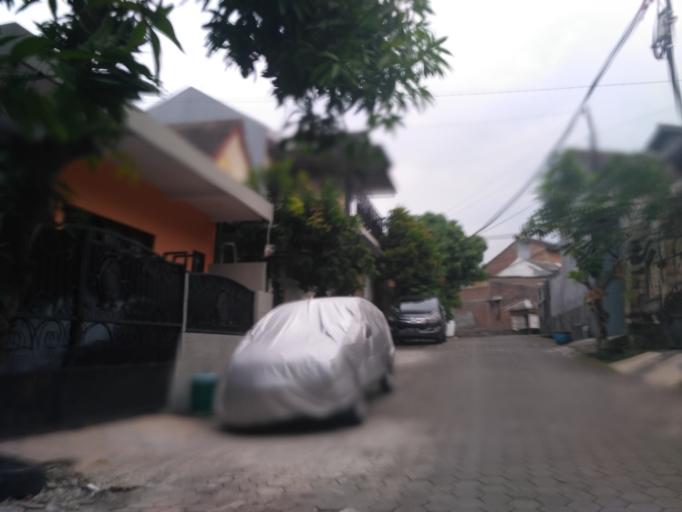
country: ID
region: Central Java
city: Mranggen
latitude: -7.0397
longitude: 110.4712
